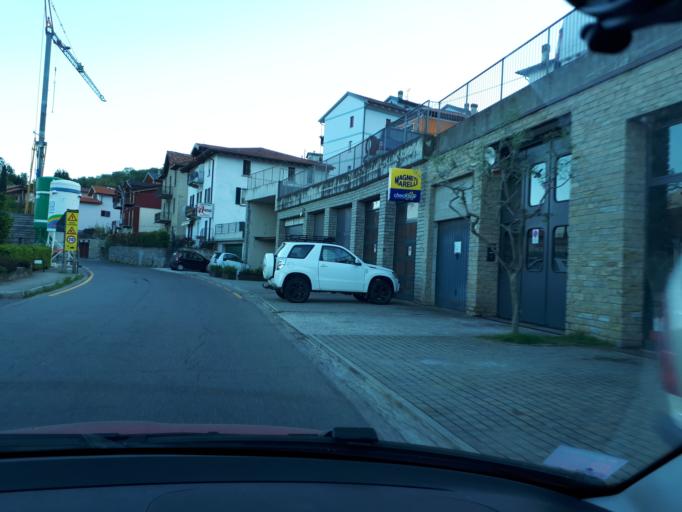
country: IT
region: Lombardy
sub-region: Provincia di Como
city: Calozzo
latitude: 46.1002
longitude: 9.2759
